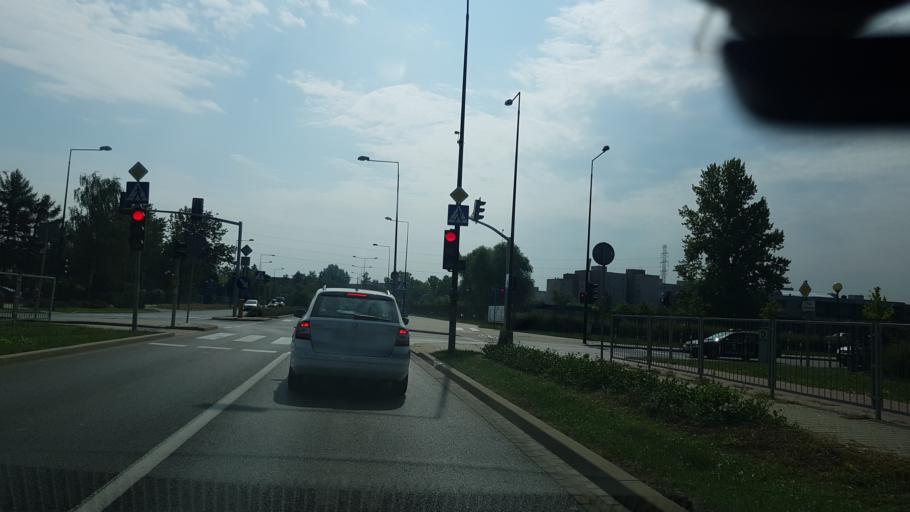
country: PL
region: Masovian Voivodeship
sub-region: Warszawa
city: Ursynow
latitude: 52.1613
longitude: 21.0490
